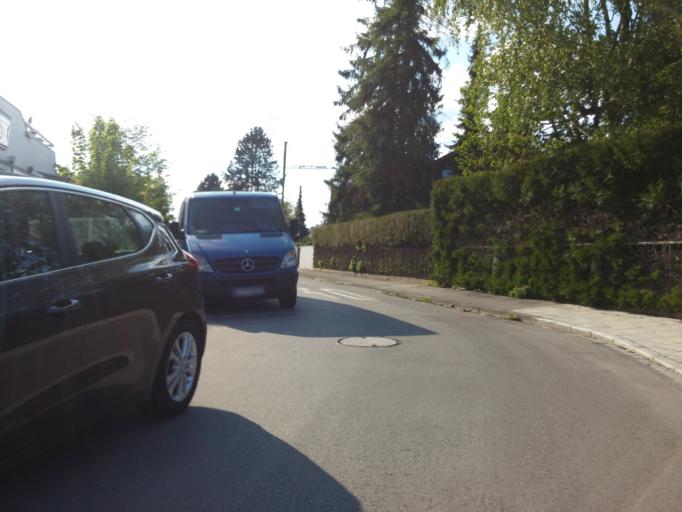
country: DE
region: Bavaria
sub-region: Upper Bavaria
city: Vaterstetten
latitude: 48.0968
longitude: 11.7672
